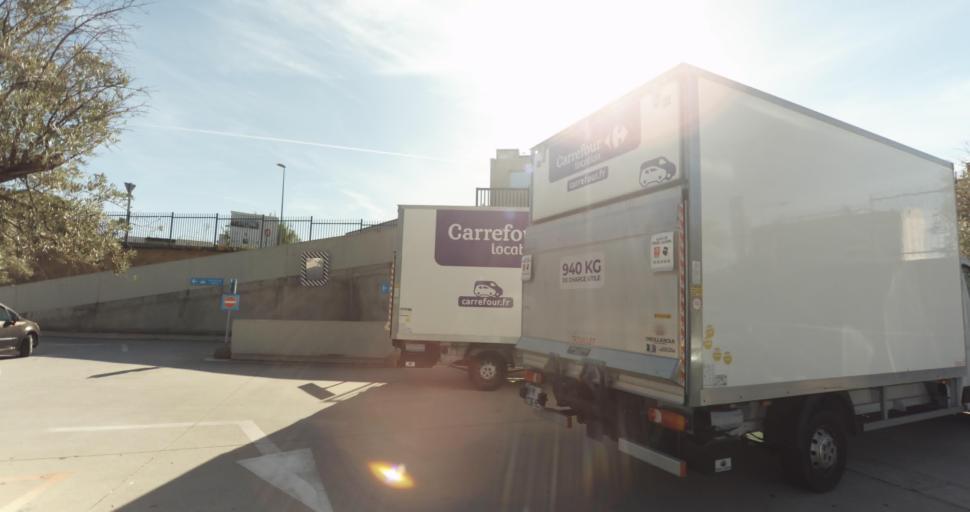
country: FR
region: Corsica
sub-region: Departement de la Corse-du-Sud
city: Ajaccio
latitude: 41.9418
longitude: 8.7462
